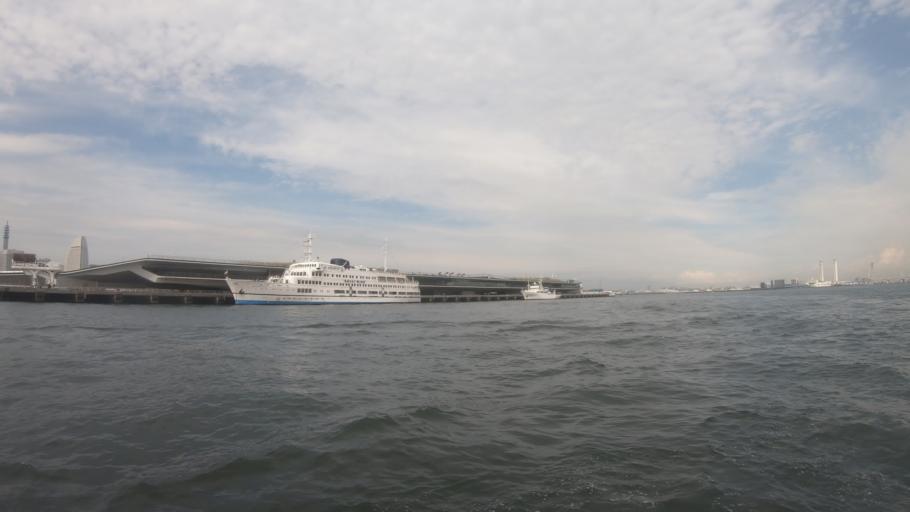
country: JP
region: Kanagawa
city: Yokohama
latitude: 35.4494
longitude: 139.6483
